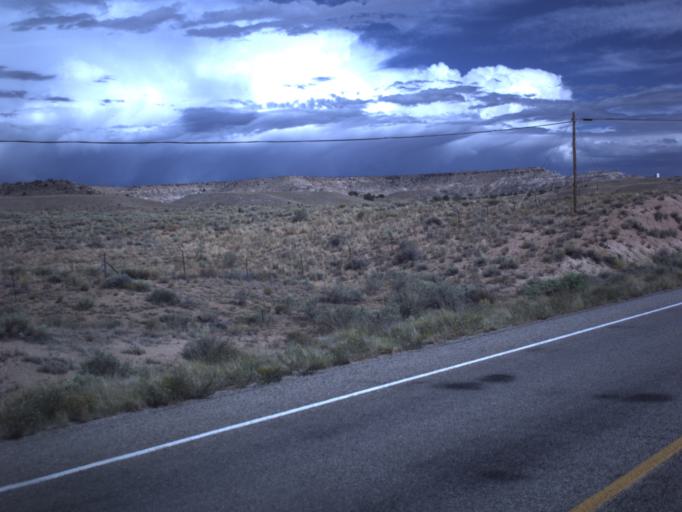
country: US
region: Colorado
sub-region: Montezuma County
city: Towaoc
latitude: 37.2046
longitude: -109.1608
